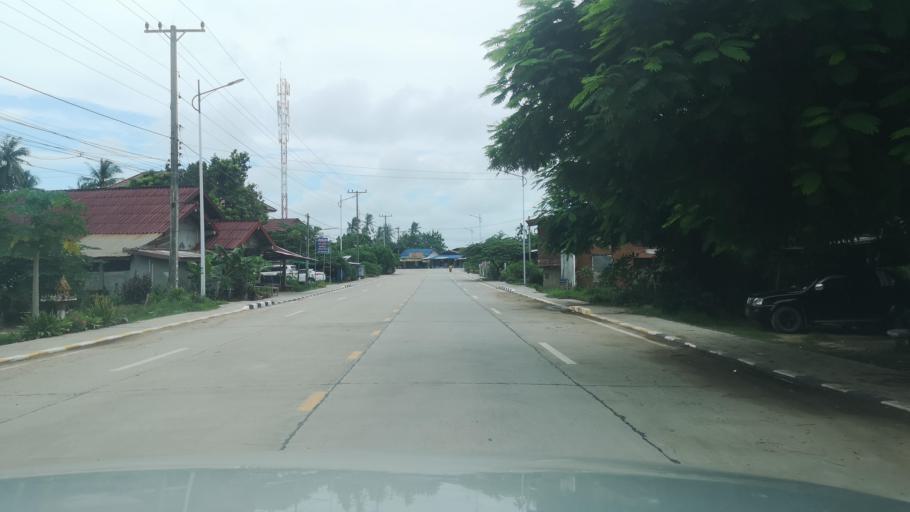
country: TH
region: Nong Khai
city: Tha Bo
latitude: 17.8110
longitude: 102.6664
